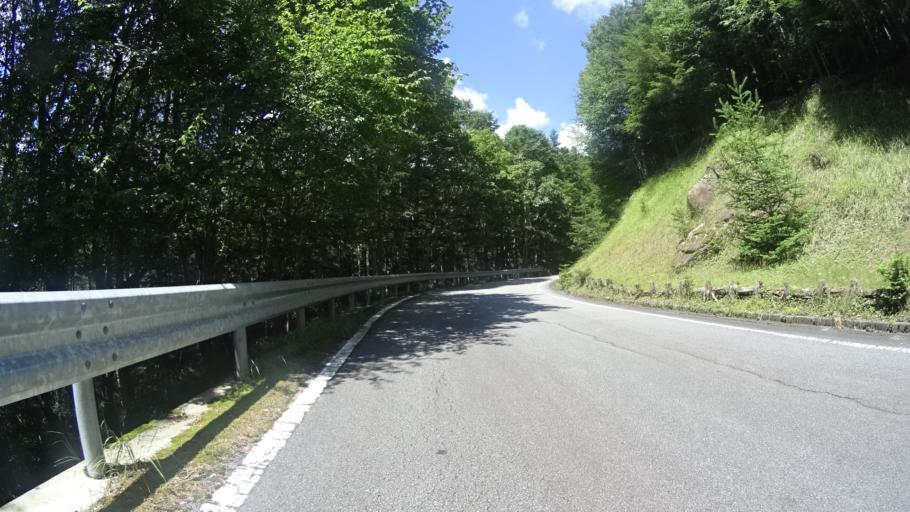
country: JP
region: Yamanashi
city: Enzan
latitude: 35.8575
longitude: 138.6453
